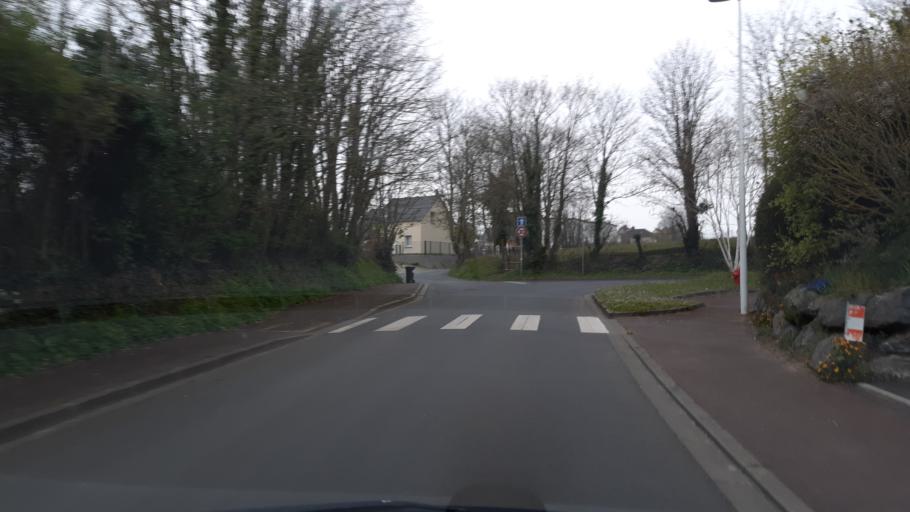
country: FR
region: Lower Normandy
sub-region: Departement de la Manche
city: Donville-les-Bains
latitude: 48.8399
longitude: -1.5724
